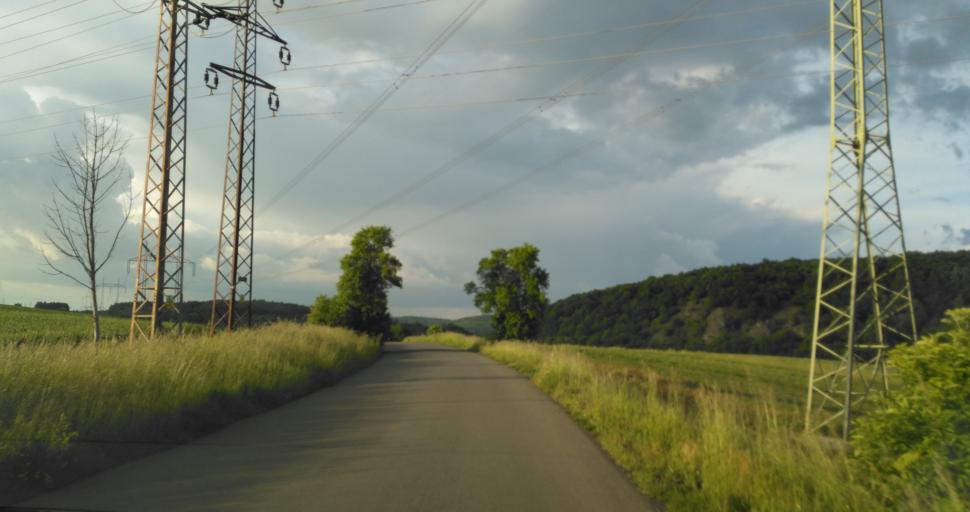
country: CZ
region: Central Bohemia
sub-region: Okres Beroun
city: Beroun
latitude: 49.9333
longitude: 14.0814
